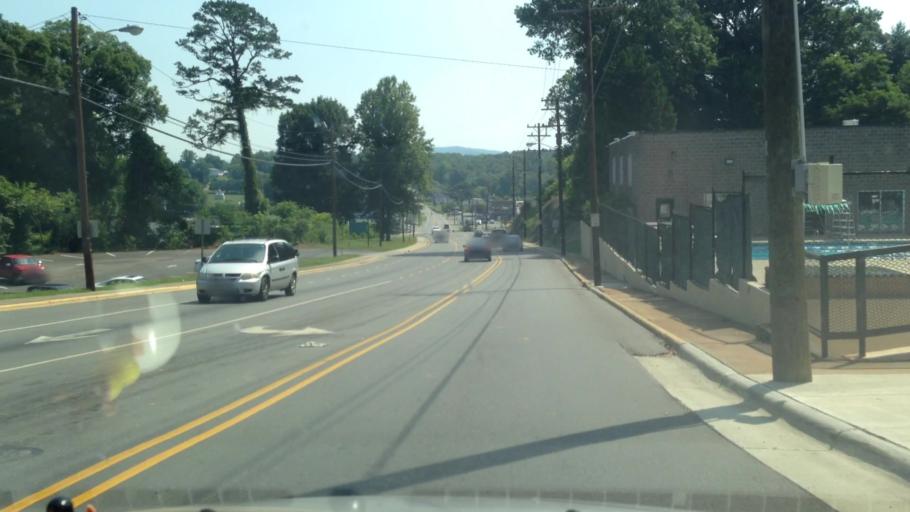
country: US
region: North Carolina
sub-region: Surry County
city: Mount Airy
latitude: 36.5000
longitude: -80.6052
